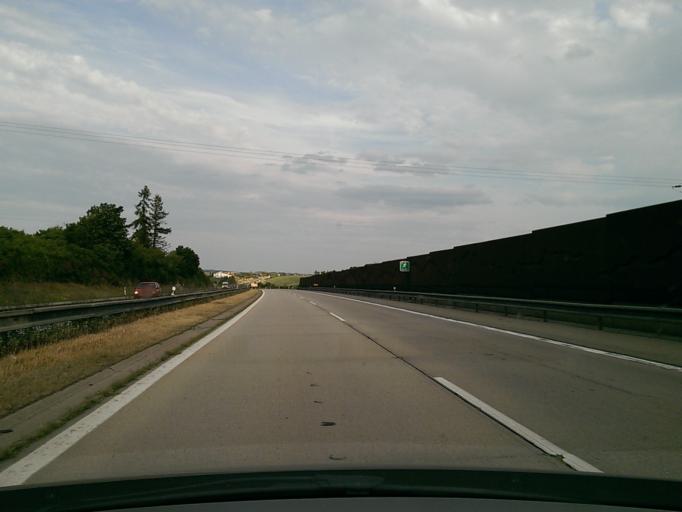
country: CZ
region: Vysocina
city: Merin
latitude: 49.3914
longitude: 15.9018
